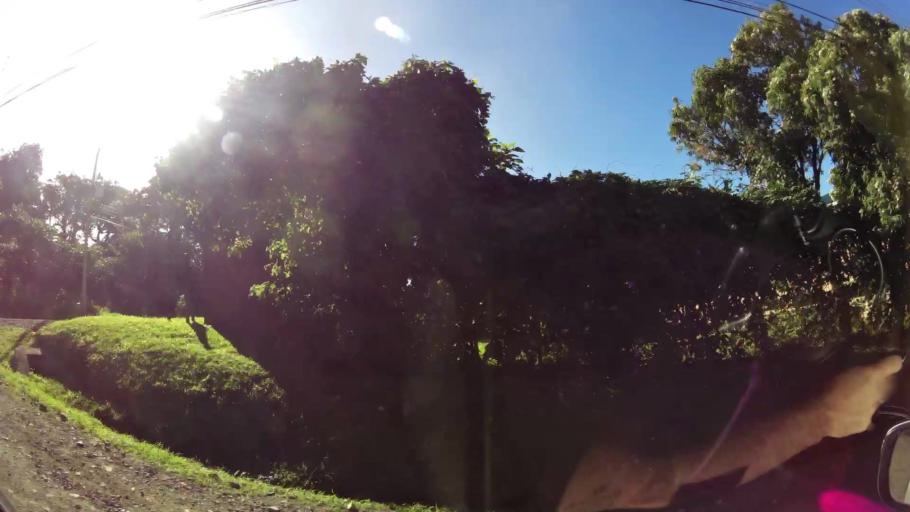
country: CR
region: Guanacaste
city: Juntas
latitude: 10.3136
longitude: -84.8190
